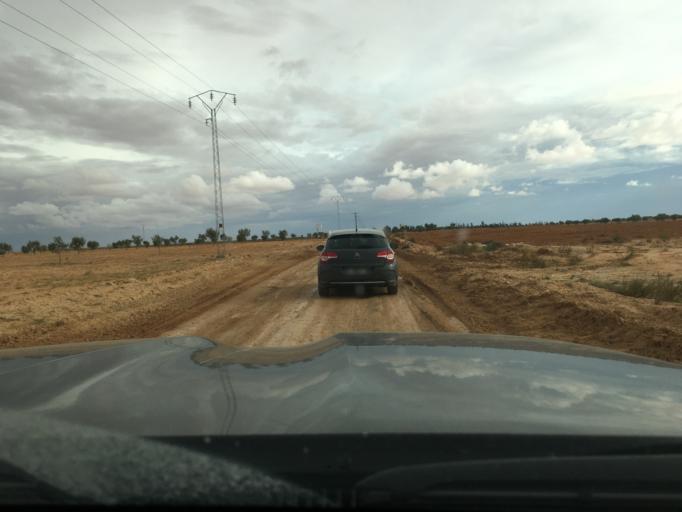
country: TN
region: Madanin
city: Medenine
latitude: 33.2790
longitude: 10.5571
